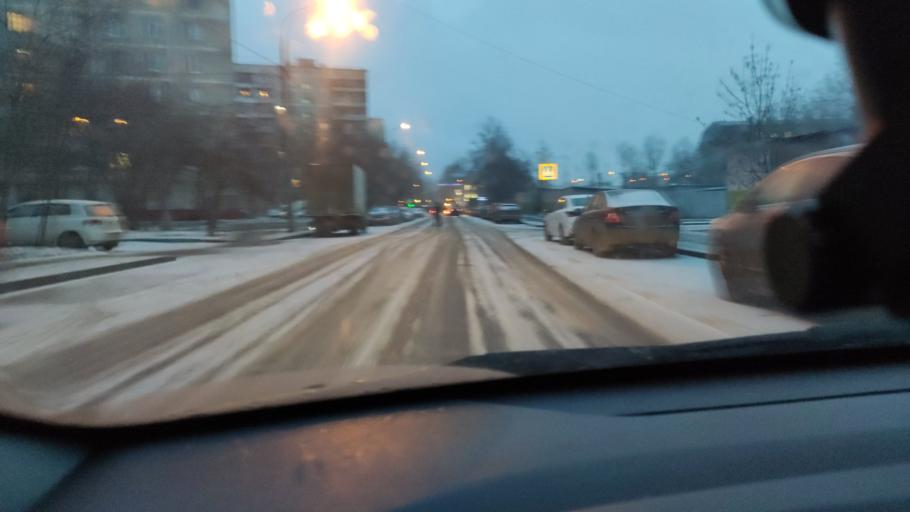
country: RU
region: Moscow
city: Annino
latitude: 55.5902
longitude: 37.6049
